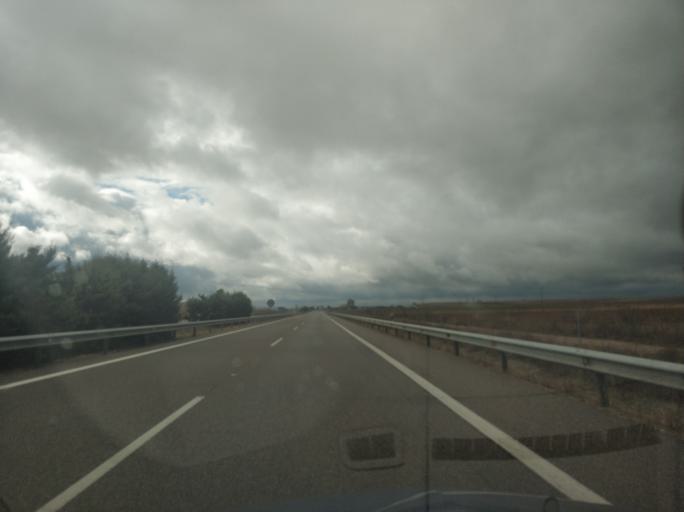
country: ES
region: Castille and Leon
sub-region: Provincia de Palencia
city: Torquemada
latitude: 42.0236
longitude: -4.3334
